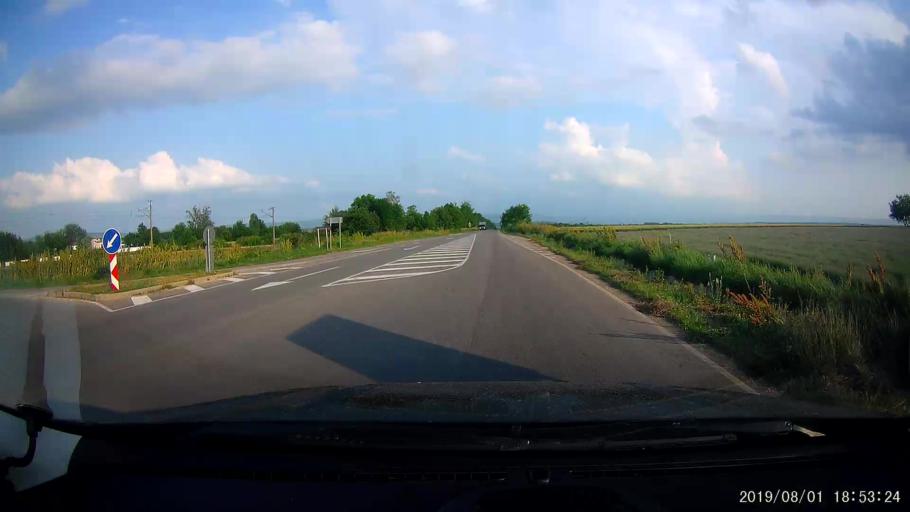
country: BG
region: Shumen
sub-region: Obshtina Shumen
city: Shumen
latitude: 43.2216
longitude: 26.9931
